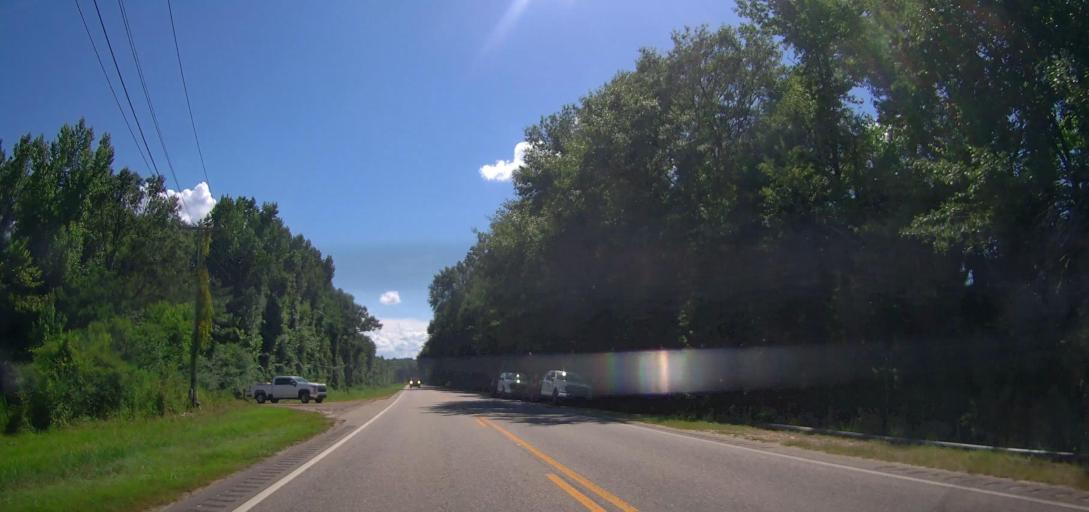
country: US
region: Alabama
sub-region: Macon County
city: Tuskegee
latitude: 32.3823
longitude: -85.8250
